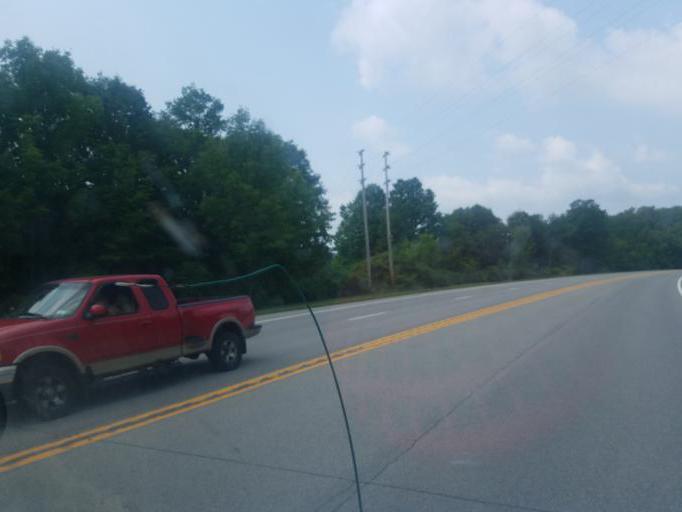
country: US
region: New York
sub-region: Herkimer County
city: Little Falls
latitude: 43.0358
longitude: -74.8150
